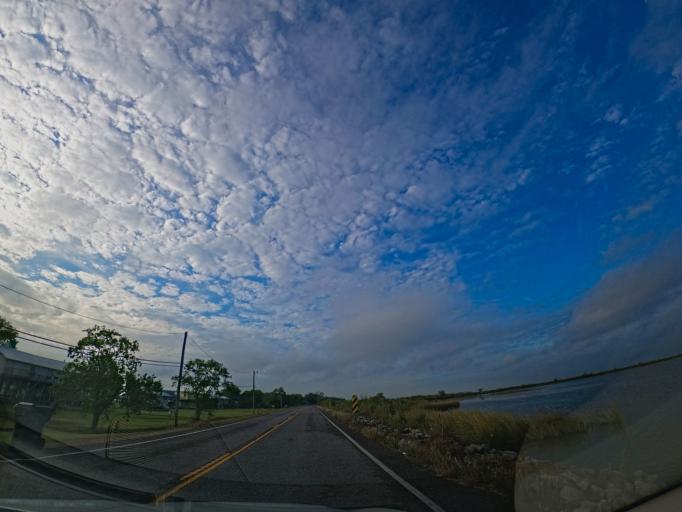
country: US
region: Louisiana
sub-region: Terrebonne Parish
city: Chauvin
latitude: 29.3734
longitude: -90.6240
